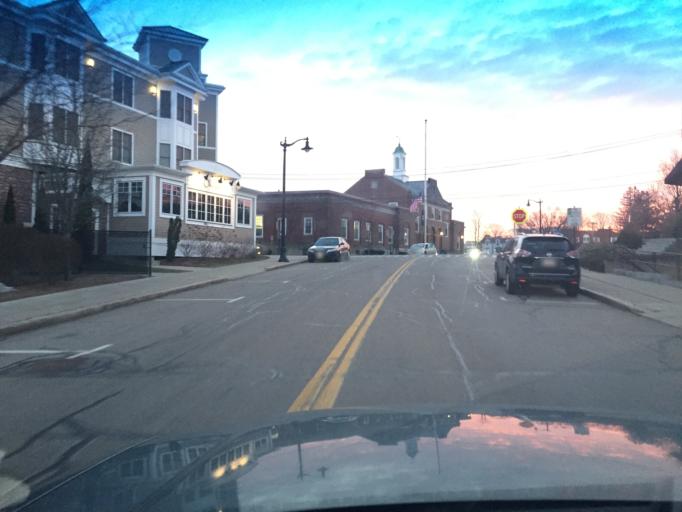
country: US
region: Massachusetts
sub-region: Norfolk County
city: Norwood
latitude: 42.1911
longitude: -71.2012
